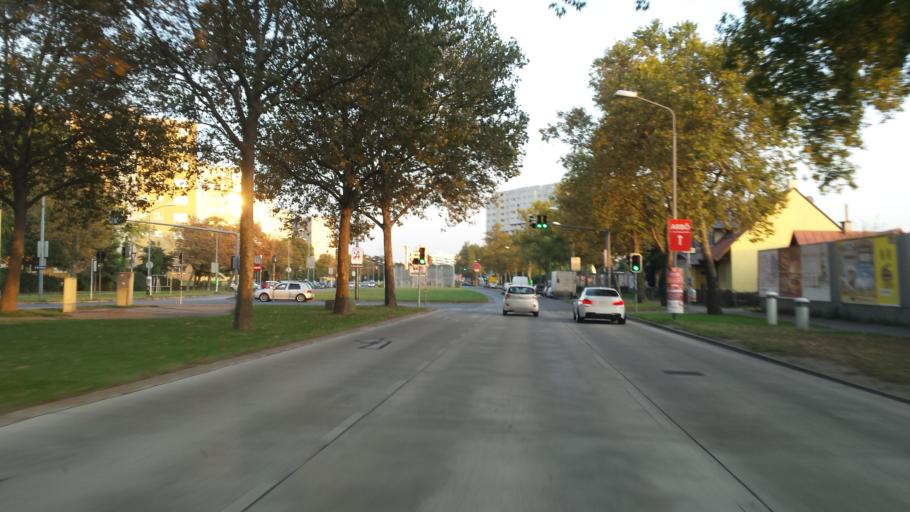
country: AT
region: Lower Austria
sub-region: Politischer Bezirk Wien-Umgebung
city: Gerasdorf bei Wien
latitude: 48.2399
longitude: 16.4368
